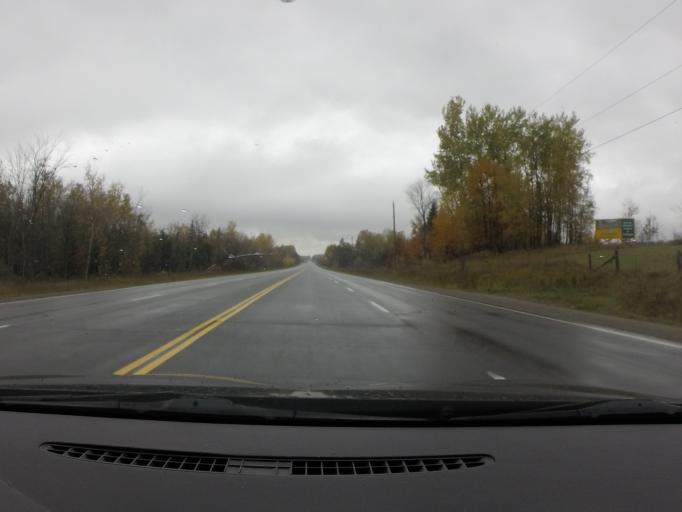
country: CA
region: Ontario
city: Belleville
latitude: 44.5314
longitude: -77.3928
